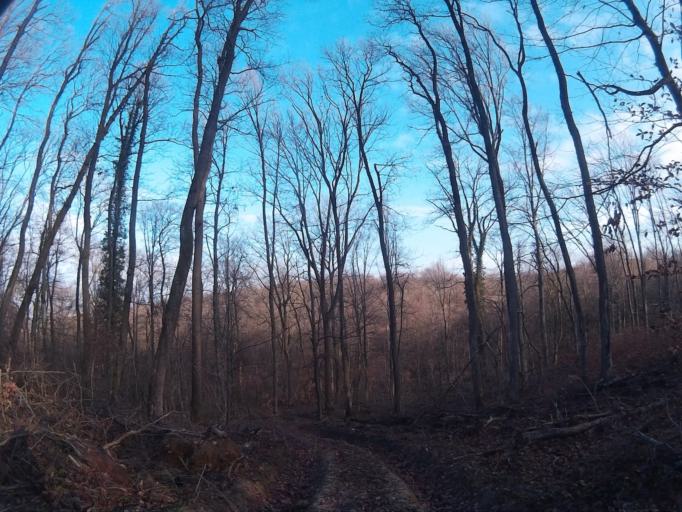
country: HU
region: Veszprem
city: Urkut
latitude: 47.1347
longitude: 17.6503
